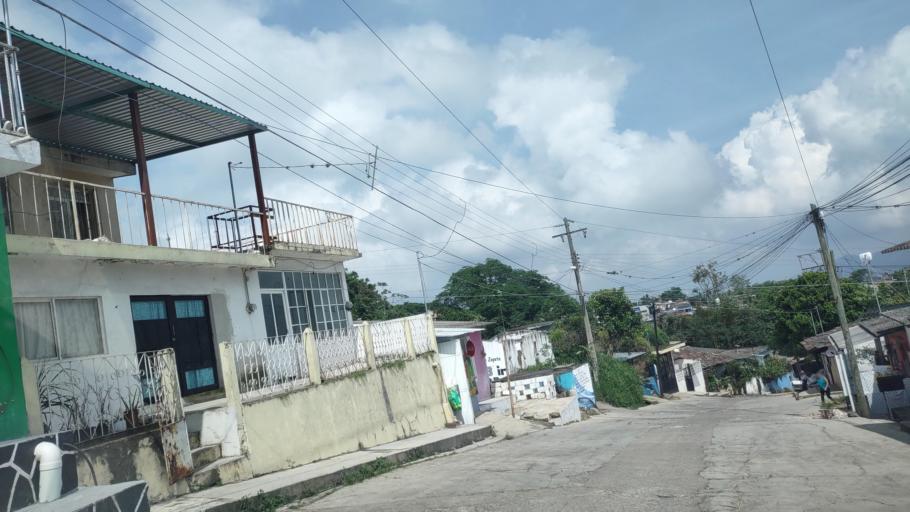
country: MX
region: Veracruz
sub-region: Emiliano Zapata
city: Jacarandas
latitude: 19.4688
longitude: -96.8376
